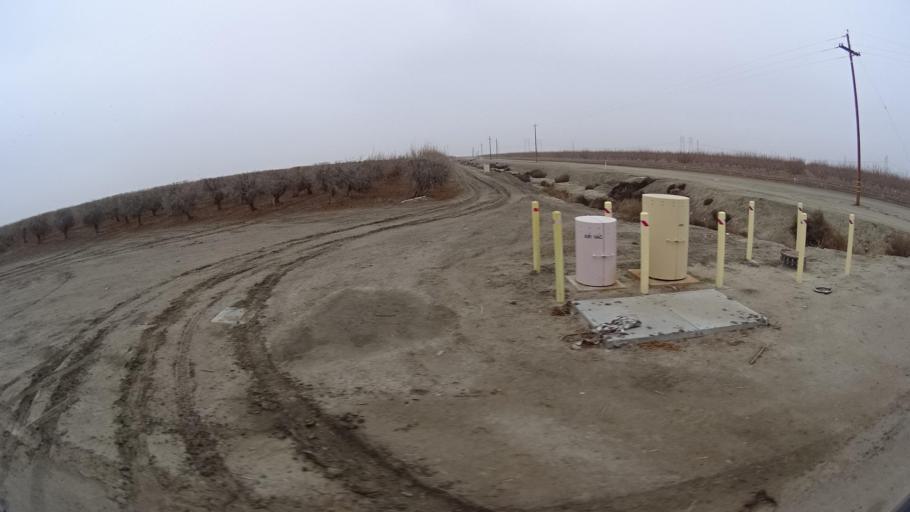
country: US
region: California
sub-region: Kern County
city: Lost Hills
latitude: 35.5868
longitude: -119.6143
